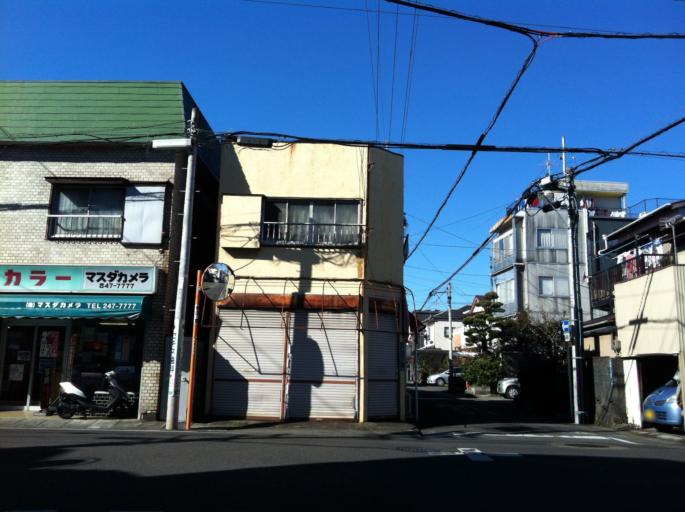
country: JP
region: Shizuoka
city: Shizuoka-shi
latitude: 34.9849
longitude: 138.3860
